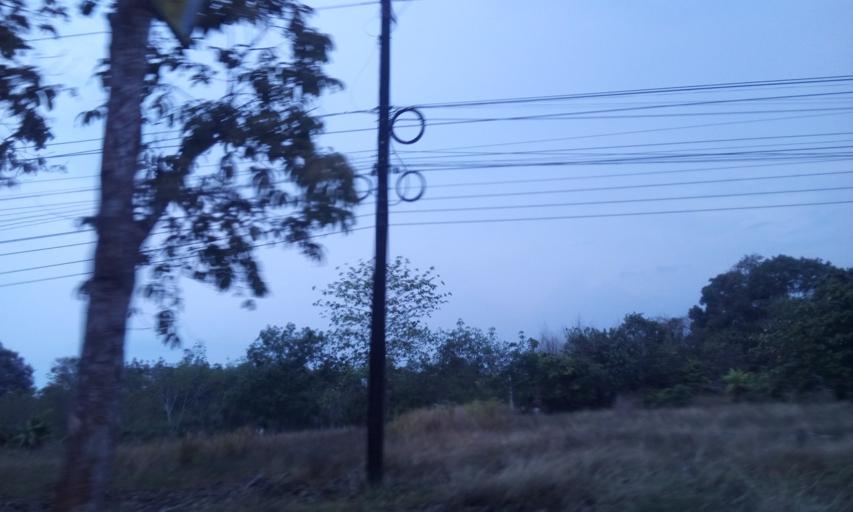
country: TH
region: Trat
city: Khao Saming
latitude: 12.3467
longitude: 102.3774
